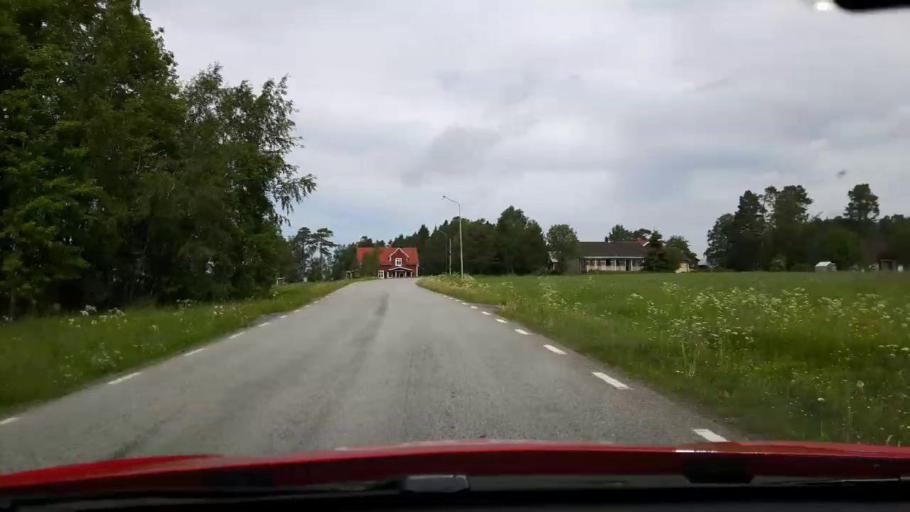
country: SE
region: Jaemtland
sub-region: OEstersunds Kommun
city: Ostersund
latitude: 63.0471
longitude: 14.4529
